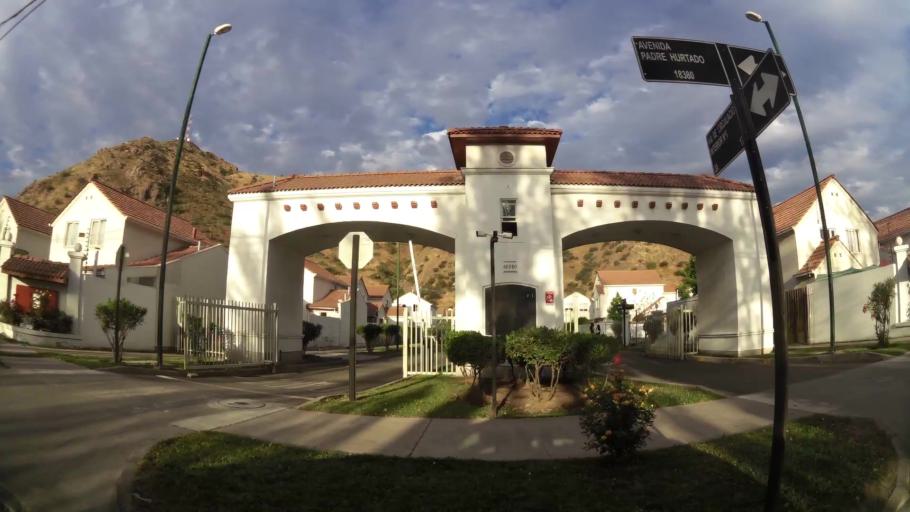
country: CL
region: Santiago Metropolitan
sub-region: Provincia de Maipo
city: San Bernardo
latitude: -33.6294
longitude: -70.6782
